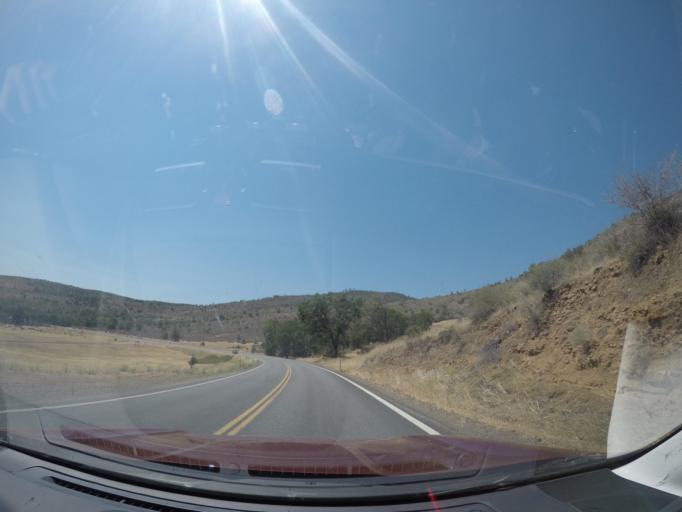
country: US
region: California
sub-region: Shasta County
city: Burney
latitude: 41.0018
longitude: -121.5033
